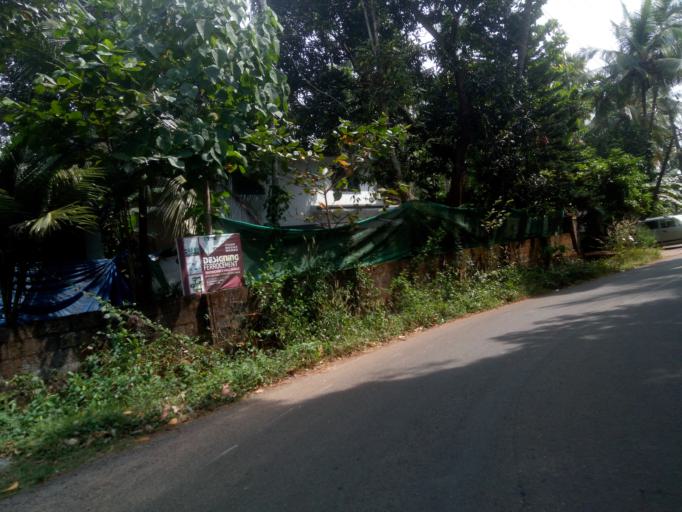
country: IN
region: Kerala
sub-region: Malappuram
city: Ponnani
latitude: 10.8040
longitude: 76.0340
